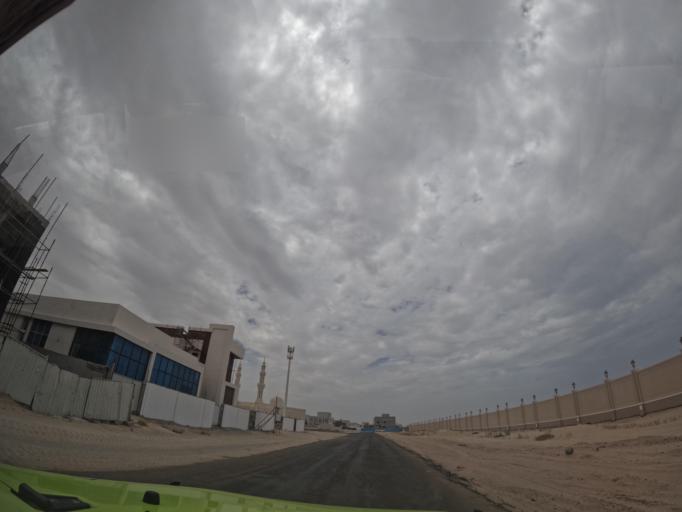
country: AE
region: Ash Shariqah
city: Sharjah
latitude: 25.1511
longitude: 55.3708
